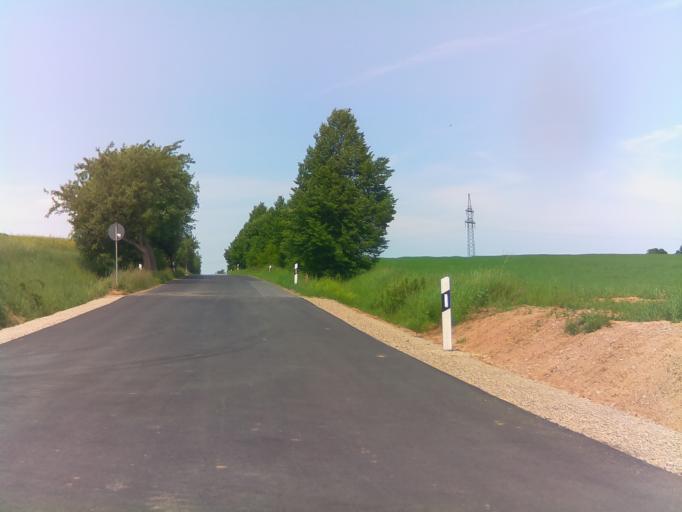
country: DE
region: Thuringia
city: Behringen
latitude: 50.7568
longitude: 11.0363
